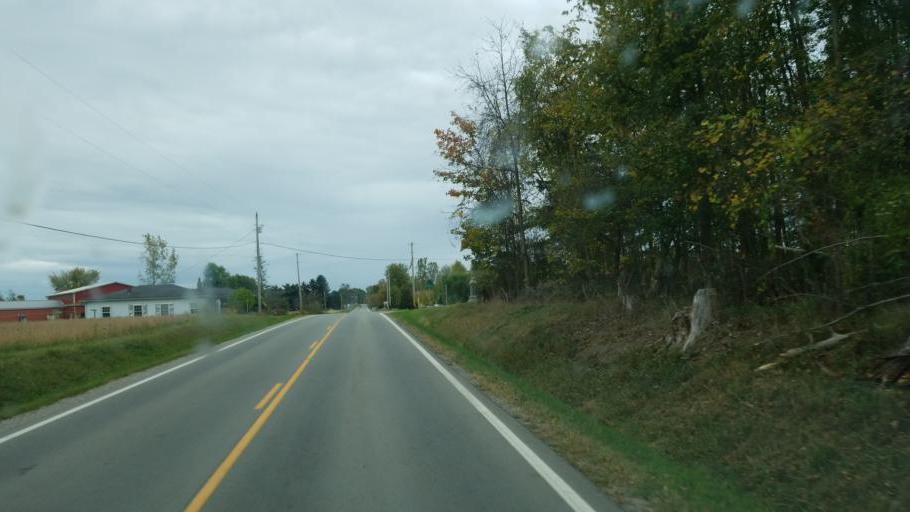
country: US
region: Ohio
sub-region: Huron County
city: New London
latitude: 41.1313
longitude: -82.4093
